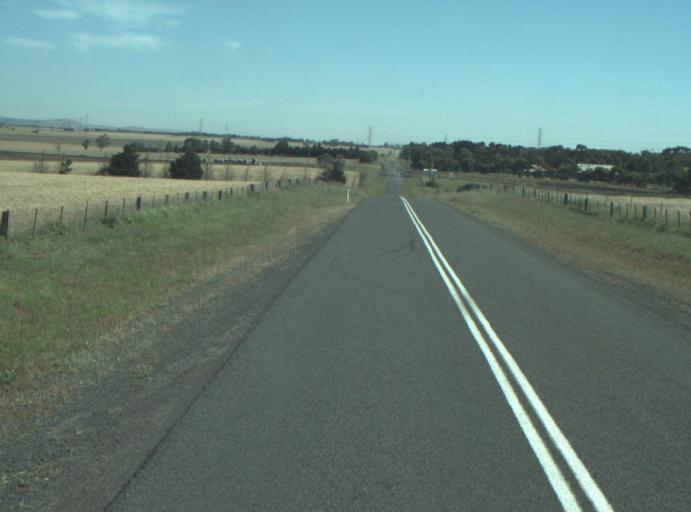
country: AU
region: Victoria
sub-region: Greater Geelong
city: Bell Post Hill
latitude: -38.0807
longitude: 144.3078
